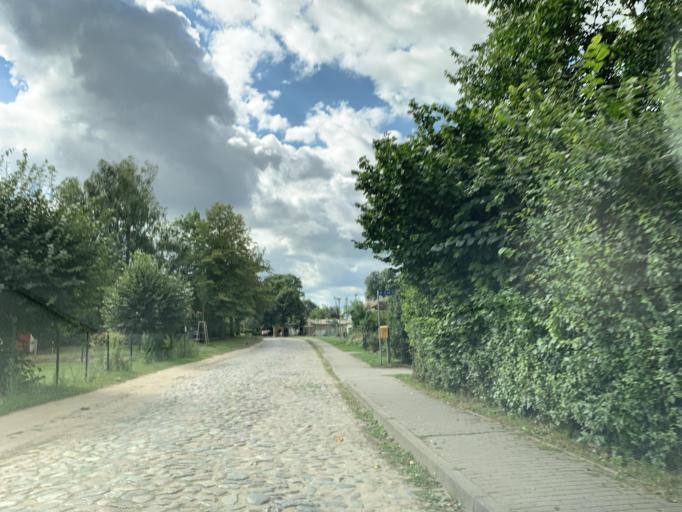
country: DE
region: Mecklenburg-Vorpommern
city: Blankensee
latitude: 53.4083
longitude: 13.2294
